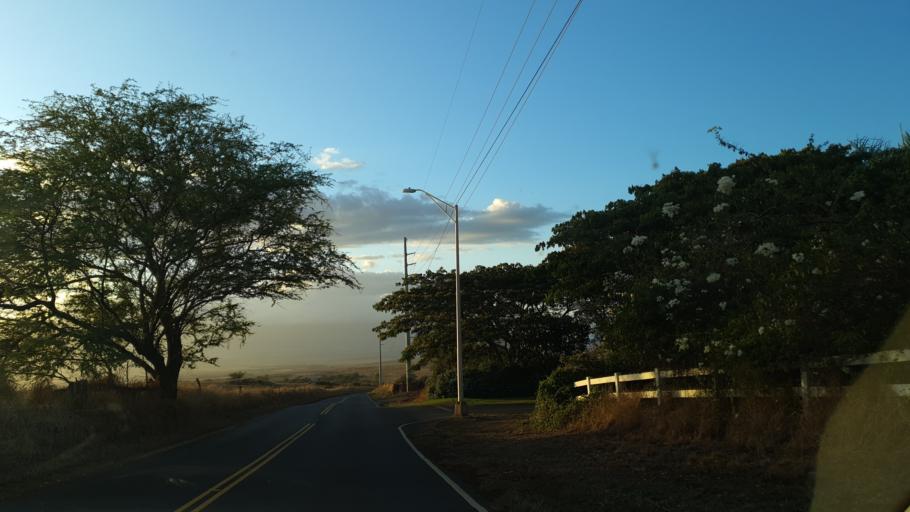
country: US
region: Hawaii
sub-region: Maui County
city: Pukalani
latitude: 20.7995
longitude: -156.3725
